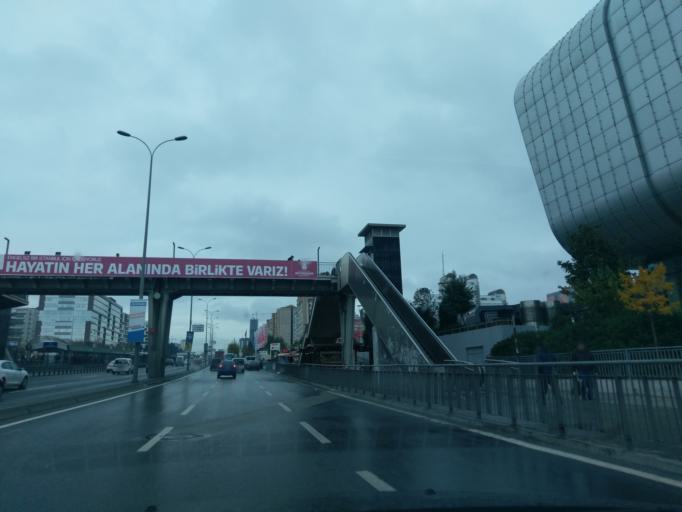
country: TR
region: Istanbul
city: Esenyurt
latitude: 41.0095
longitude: 28.6580
